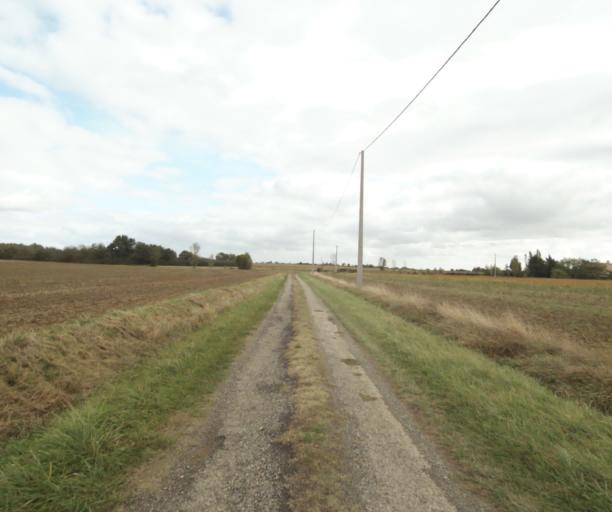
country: FR
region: Midi-Pyrenees
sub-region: Departement du Tarn-et-Garonne
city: Finhan
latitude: 43.8918
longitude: 1.1098
